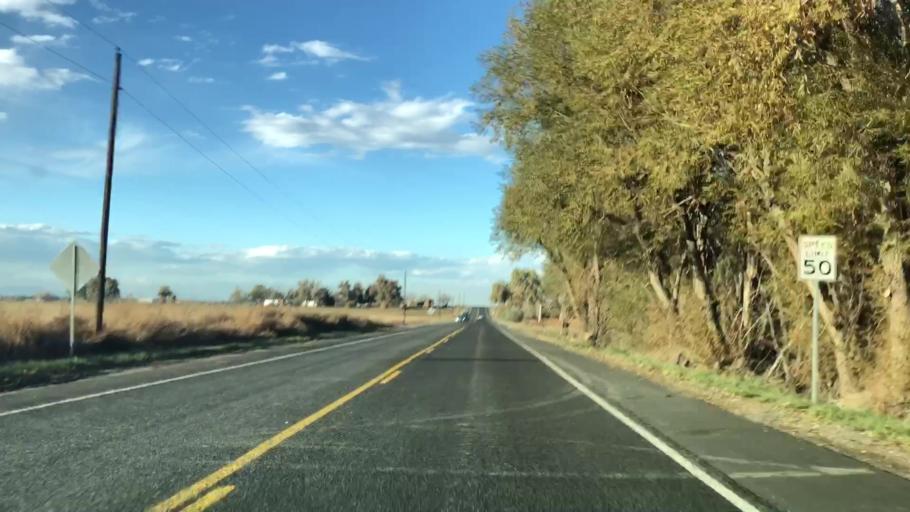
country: US
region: Colorado
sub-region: Larimer County
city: Loveland
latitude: 40.4680
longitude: -105.0203
